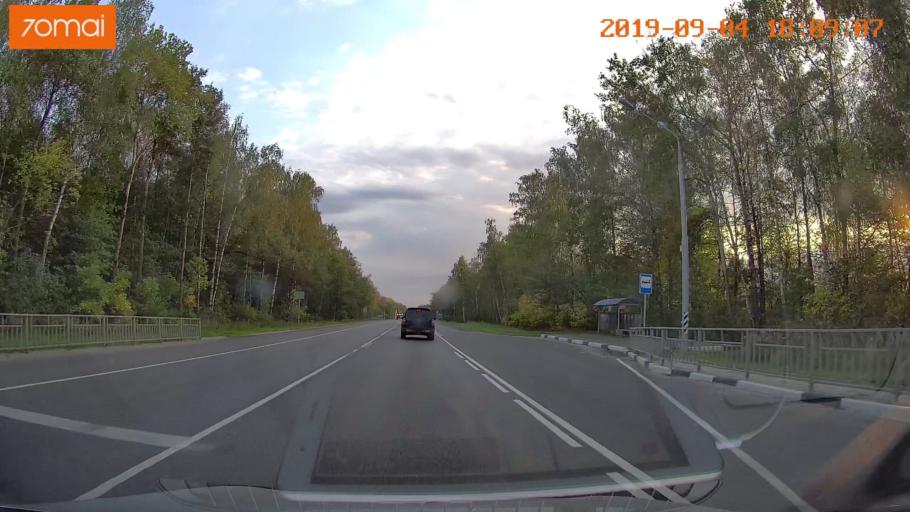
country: RU
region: Moskovskaya
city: Khorlovo
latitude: 55.3986
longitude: 38.7777
